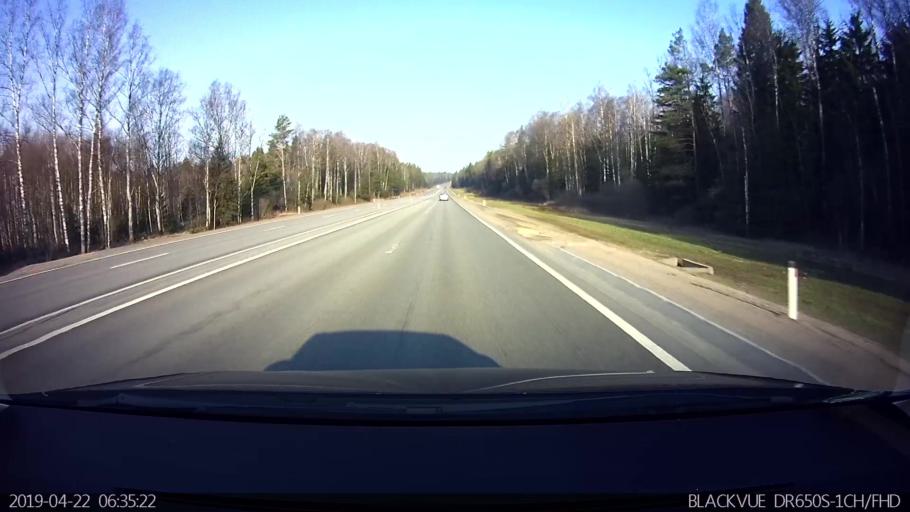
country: RU
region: Moskovskaya
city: Uvarovka
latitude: 55.4777
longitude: 35.4660
